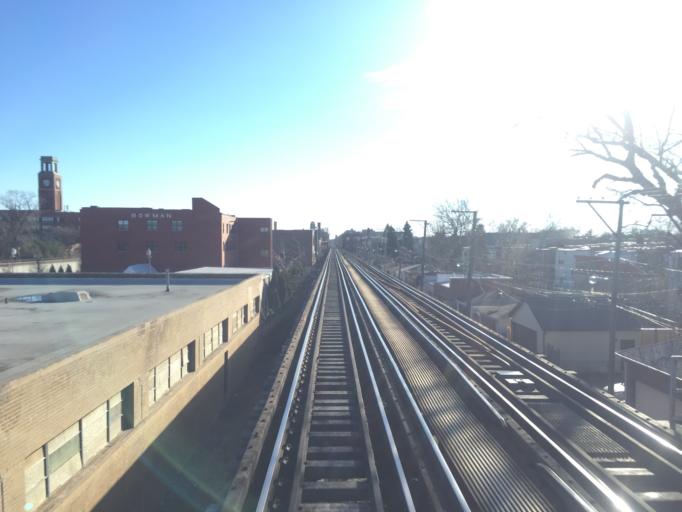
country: US
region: Illinois
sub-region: Cook County
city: Lincolnwood
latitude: 41.9605
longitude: -87.6751
